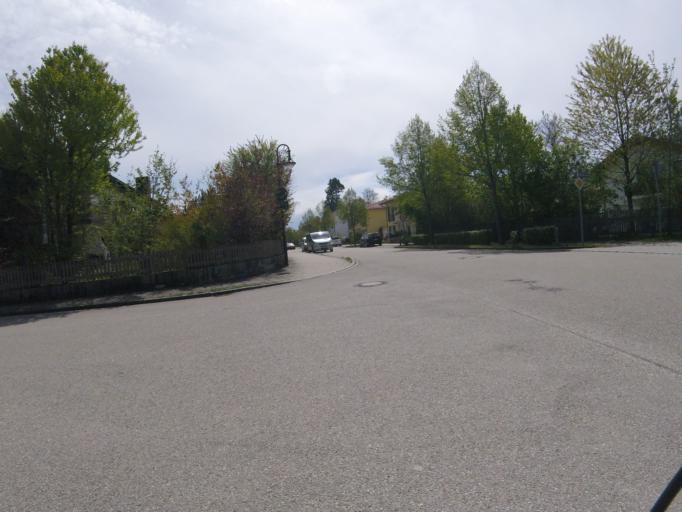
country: DE
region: Bavaria
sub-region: Upper Bavaria
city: Hohenbrunn
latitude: 48.0337
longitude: 11.7057
